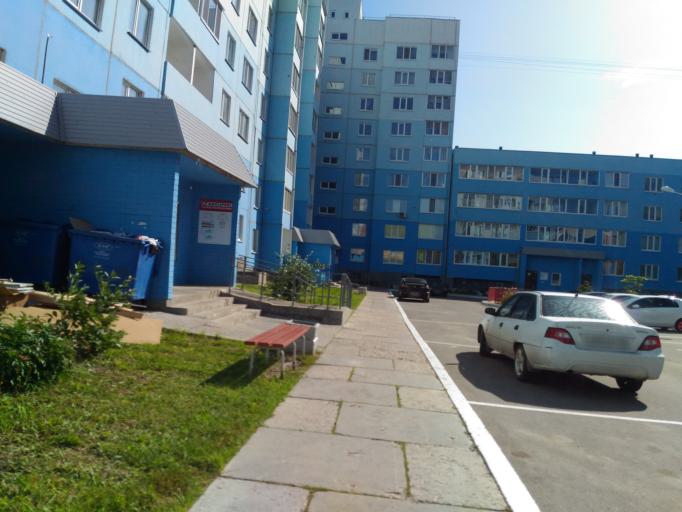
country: RU
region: Ulyanovsk
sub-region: Ulyanovskiy Rayon
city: Ulyanovsk
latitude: 54.3477
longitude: 48.3398
